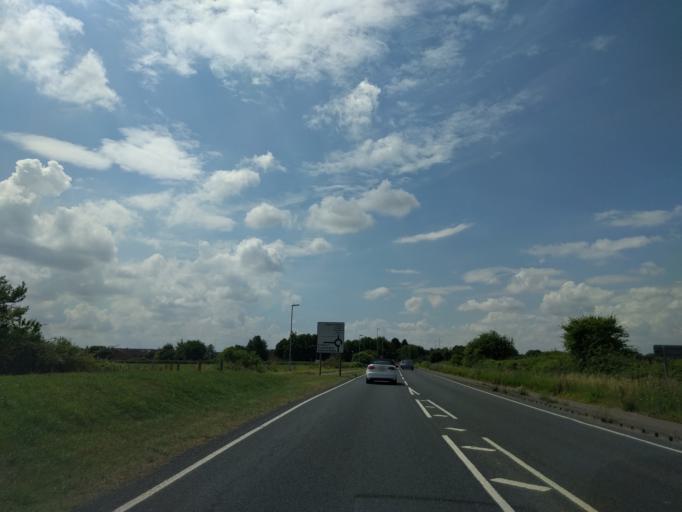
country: GB
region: England
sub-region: Cambridgeshire
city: Fulbourn
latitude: 52.1979
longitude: 0.1859
